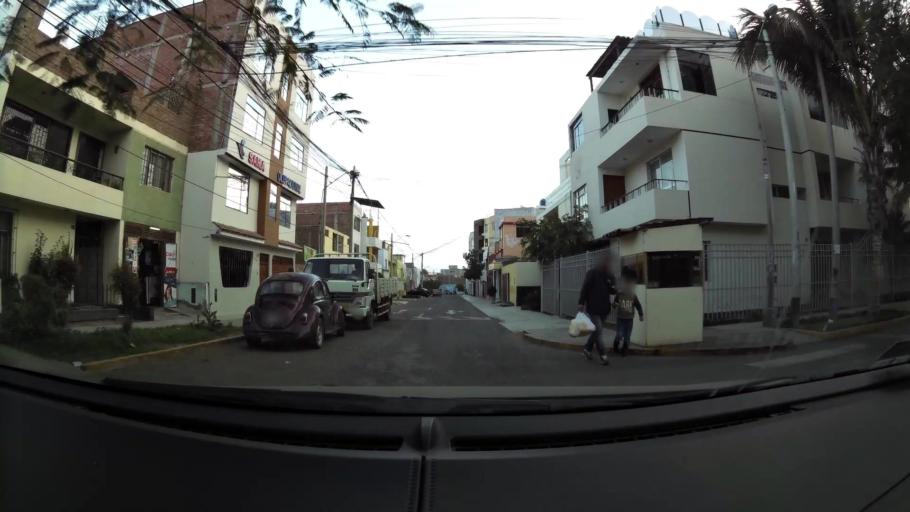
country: PE
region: La Libertad
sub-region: Provincia de Trujillo
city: Trujillo
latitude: -8.0990
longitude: -79.0356
